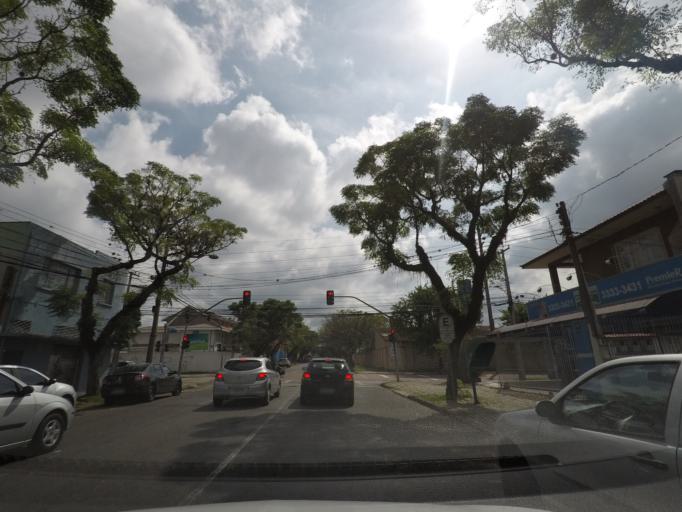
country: BR
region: Parana
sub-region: Curitiba
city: Curitiba
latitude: -25.4432
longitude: -49.2581
